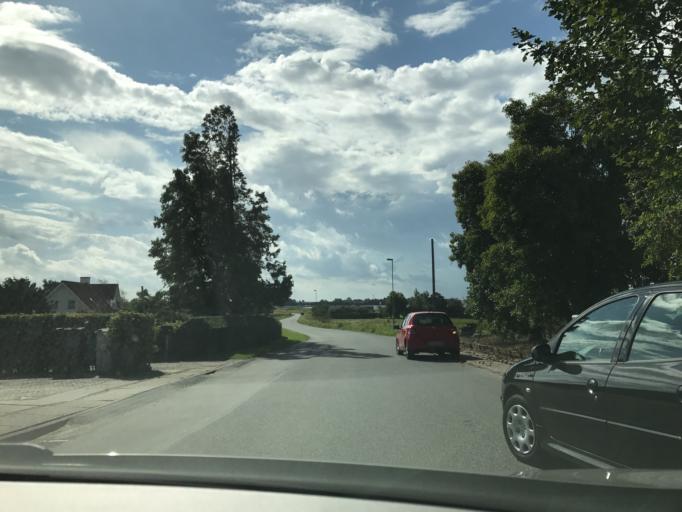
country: DK
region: South Denmark
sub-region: Middelfart Kommune
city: Norre Aby
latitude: 55.4254
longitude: 9.8297
